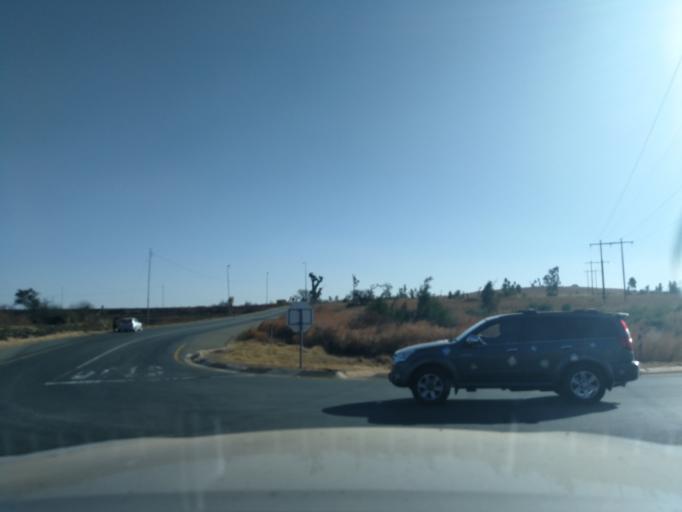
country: ZA
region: Gauteng
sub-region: West Rand District Municipality
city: Randfontein
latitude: -26.0249
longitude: 27.5898
